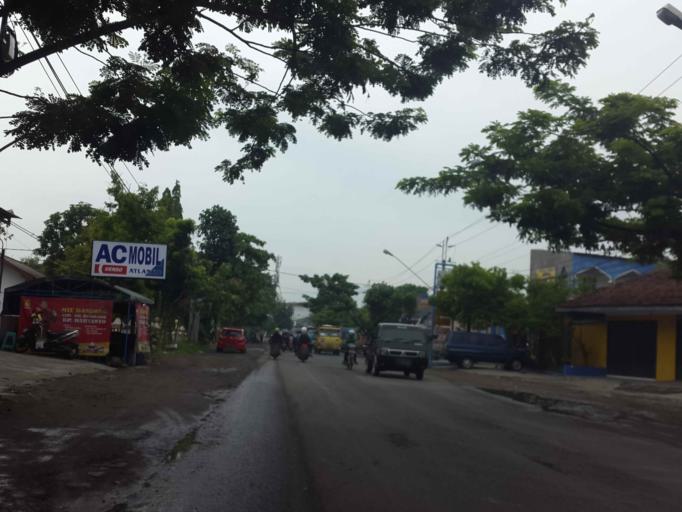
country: ID
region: Central Java
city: Mranggen
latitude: -7.0023
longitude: 110.4713
